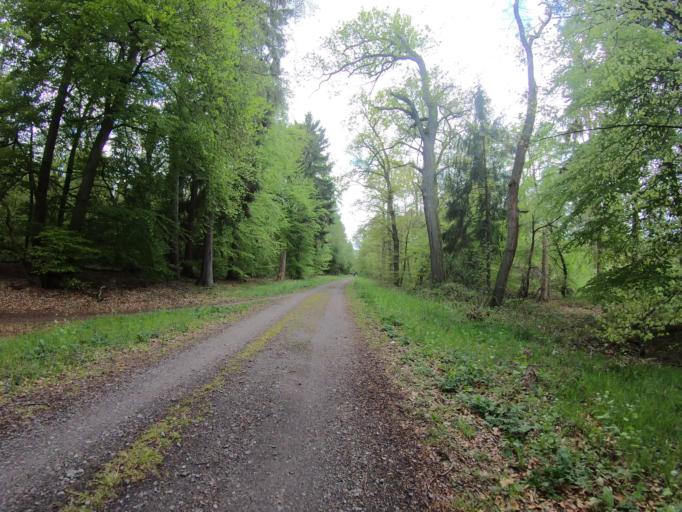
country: DE
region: Lower Saxony
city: Gifhorn
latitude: 52.5006
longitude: 10.5661
